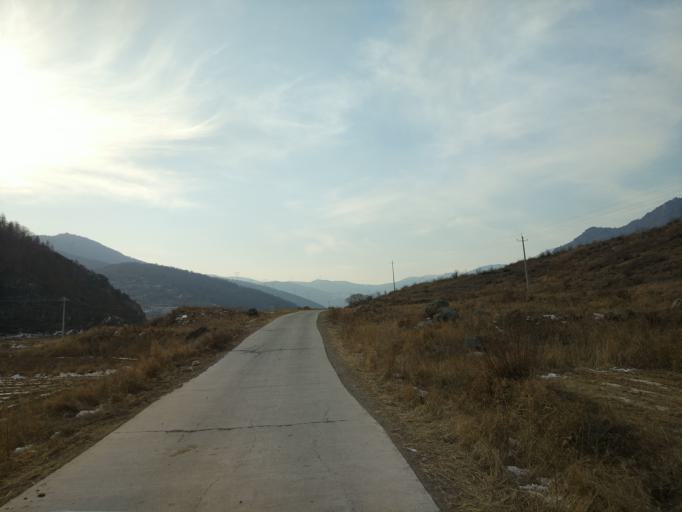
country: CN
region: Hebei
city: Xiwanzi
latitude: 40.8207
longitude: 115.4887
